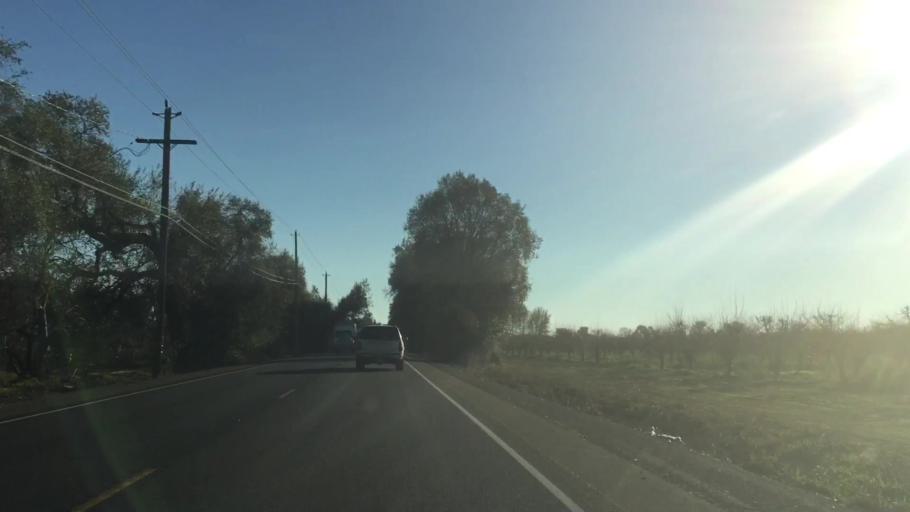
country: US
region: California
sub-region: Sutter County
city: Live Oak
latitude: 39.2784
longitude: -121.5955
